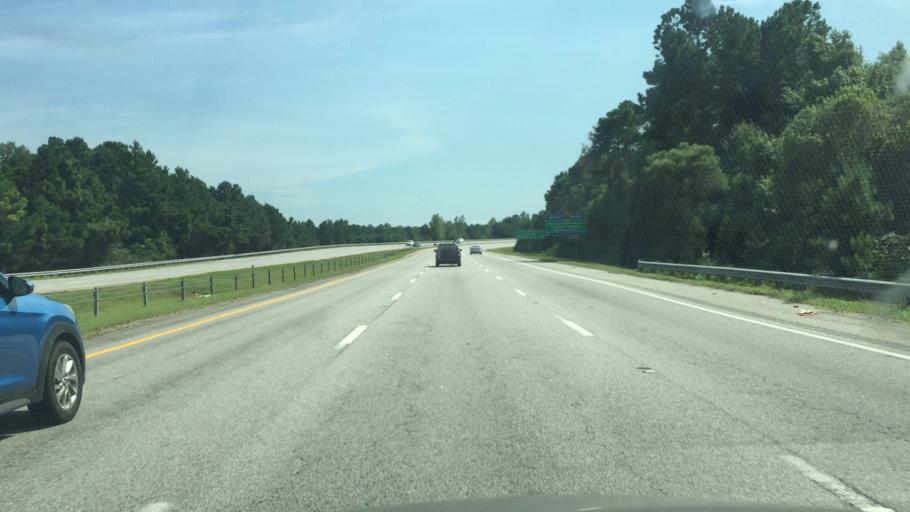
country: US
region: South Carolina
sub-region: Horry County
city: Myrtle Beach
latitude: 33.7868
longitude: -78.8045
